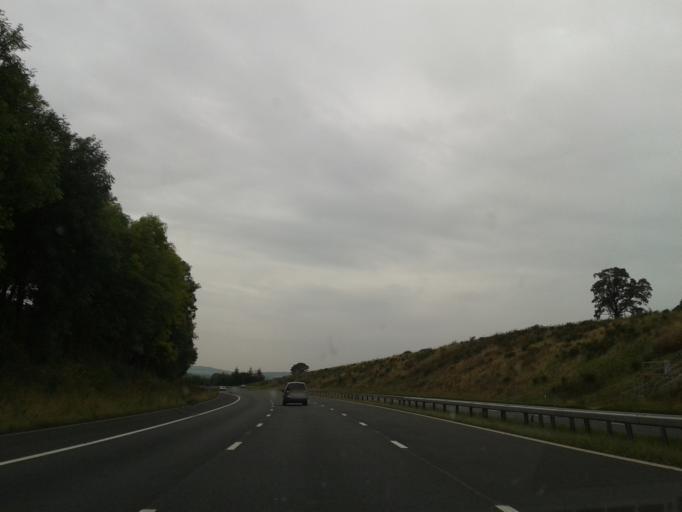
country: GB
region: England
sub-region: Cumbria
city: Milnthorpe
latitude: 54.2537
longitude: -2.6936
